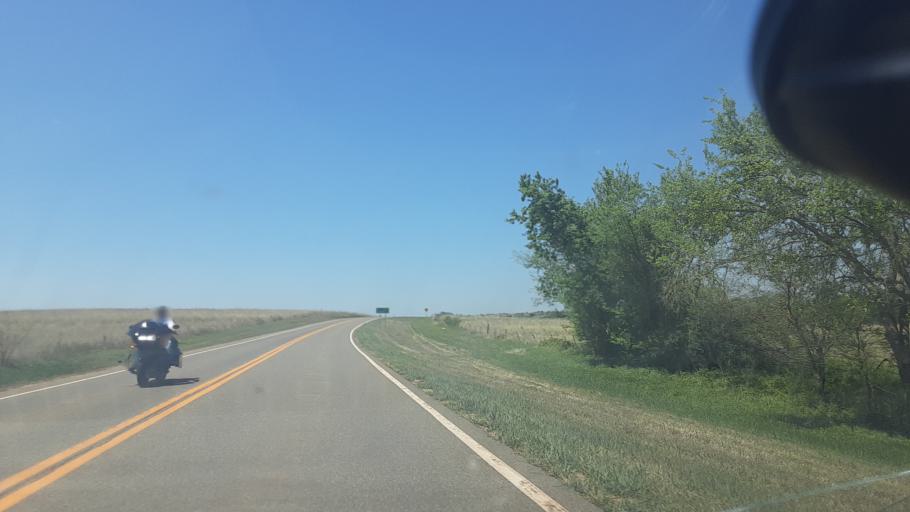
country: US
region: Oklahoma
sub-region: Noble County
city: Perry
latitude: 36.1118
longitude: -97.3814
